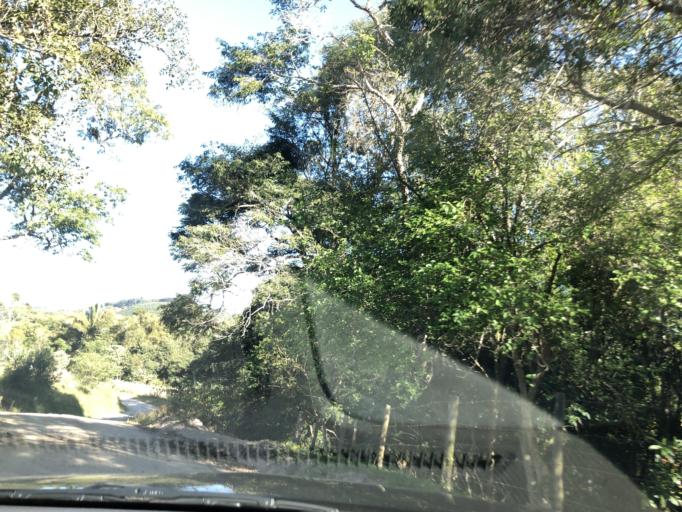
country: BR
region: Sao Paulo
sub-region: Pilar Do Sul
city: Pilar do Sul
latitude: -23.8256
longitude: -47.6282
